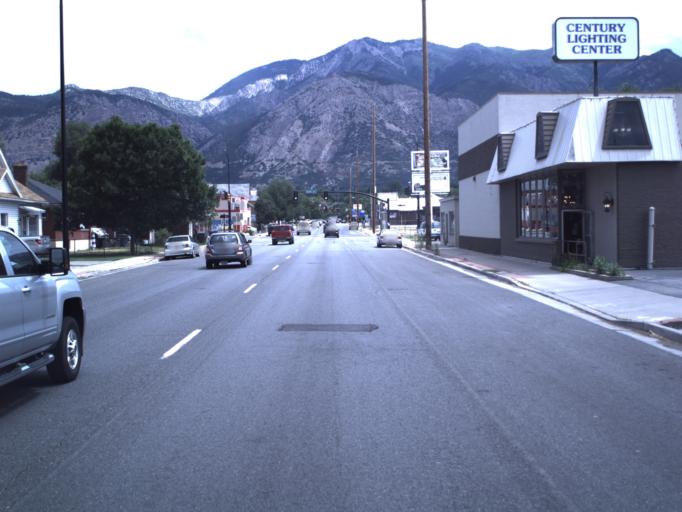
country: US
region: Utah
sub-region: Weber County
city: Ogden
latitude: 41.2082
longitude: -111.9751
